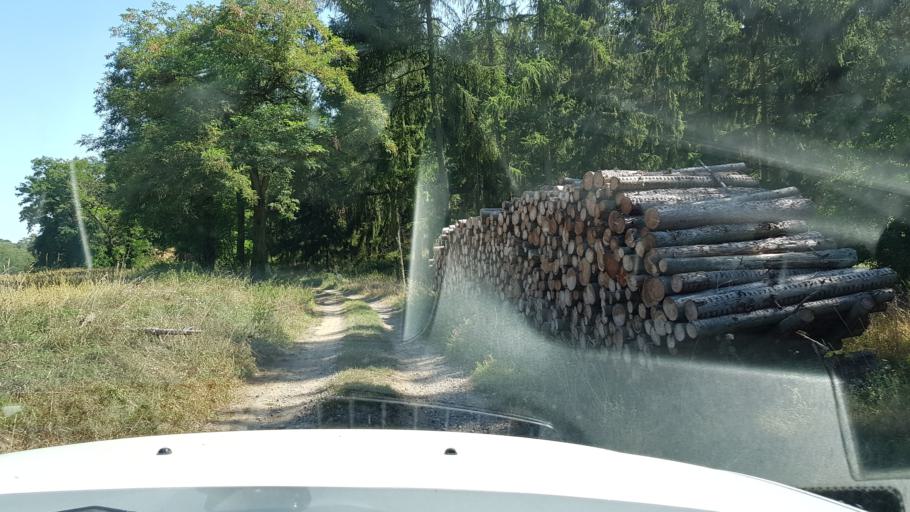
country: PL
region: West Pomeranian Voivodeship
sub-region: Powiat gryfinski
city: Cedynia
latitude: 52.8444
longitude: 14.2491
